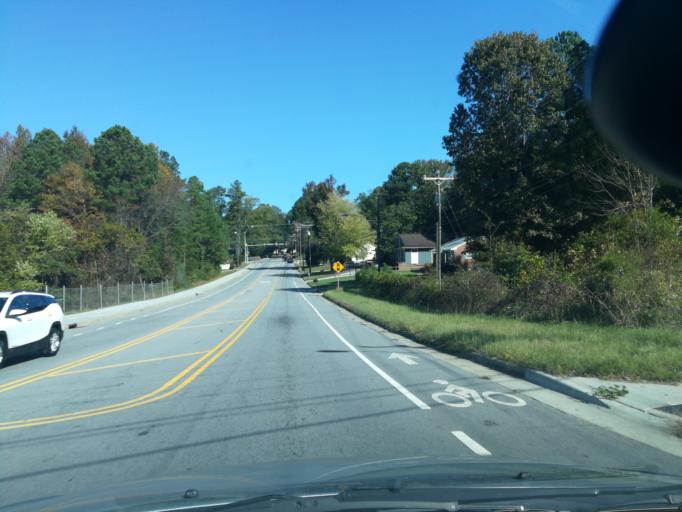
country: US
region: North Carolina
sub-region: Durham County
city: Durham
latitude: 36.0339
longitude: -78.9103
